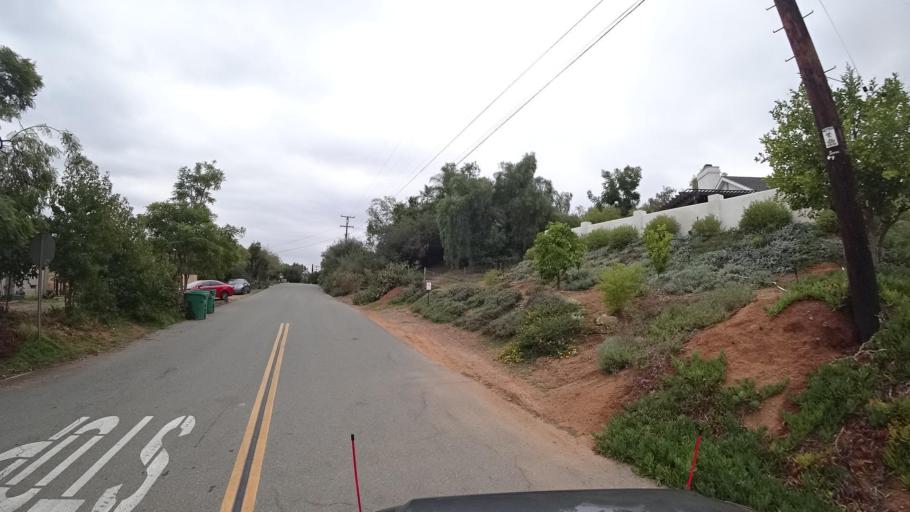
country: US
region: California
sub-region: San Diego County
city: Casa de Oro-Mount Helix
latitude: 32.7587
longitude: -116.9752
